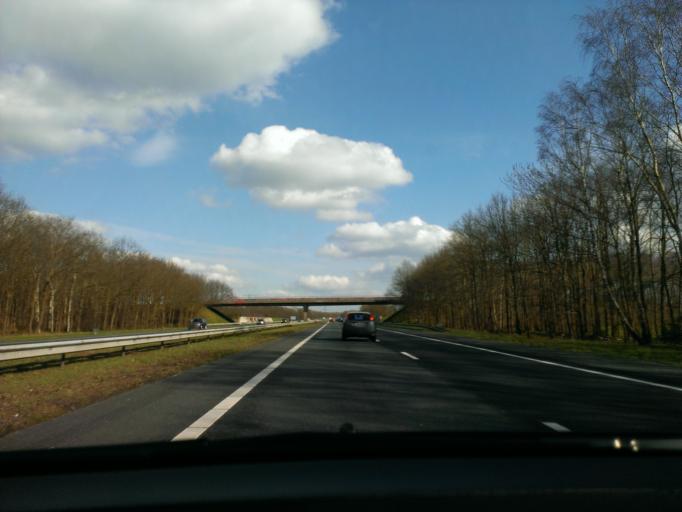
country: NL
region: Overijssel
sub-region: Gemeente Almelo
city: Almelo
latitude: 52.3186
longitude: 6.6709
